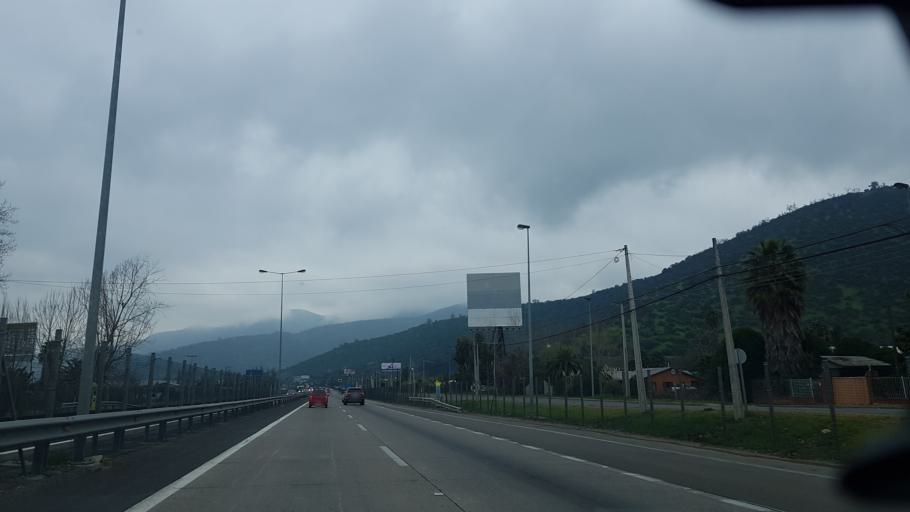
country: CL
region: Santiago Metropolitan
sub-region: Provincia de Chacabuco
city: Lampa
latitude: -33.4184
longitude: -71.0484
